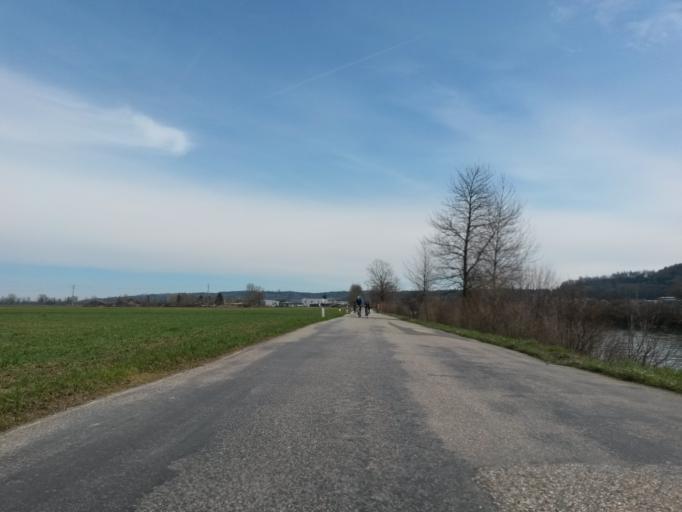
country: CH
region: Bern
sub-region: Biel/Bienne District
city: Meinisberg
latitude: 47.1430
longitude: 7.3483
